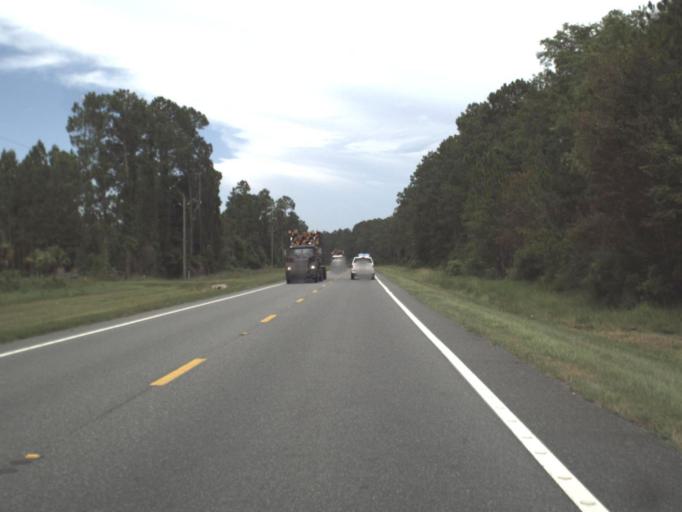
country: US
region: Florida
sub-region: Taylor County
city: Perry
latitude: 30.1008
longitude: -83.4495
